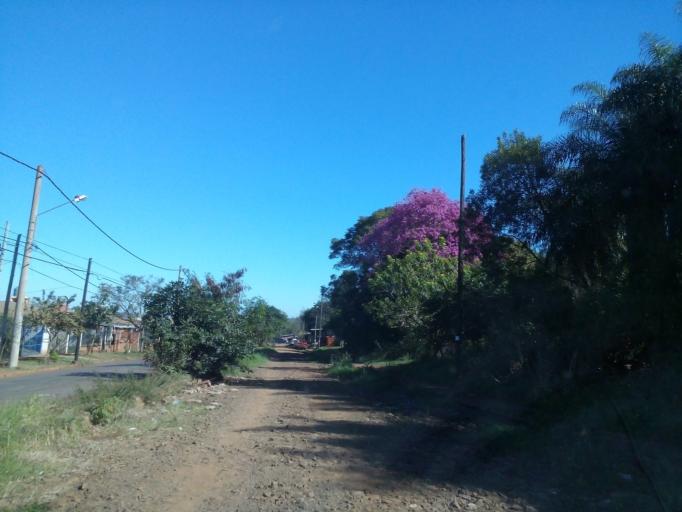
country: AR
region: Misiones
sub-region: Departamento de Capital
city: Posadas
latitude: -27.3869
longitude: -55.9384
